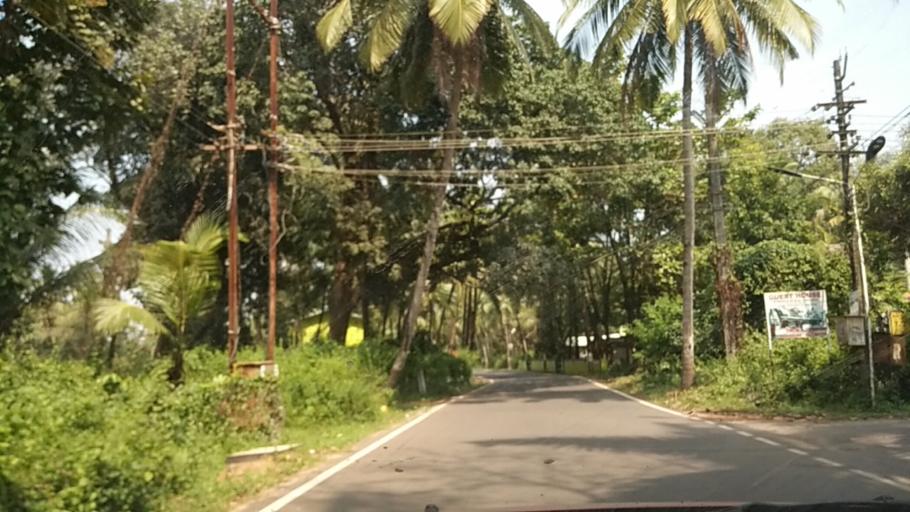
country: IN
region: Goa
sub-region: South Goa
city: Colva
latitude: 15.2879
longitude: 73.9206
